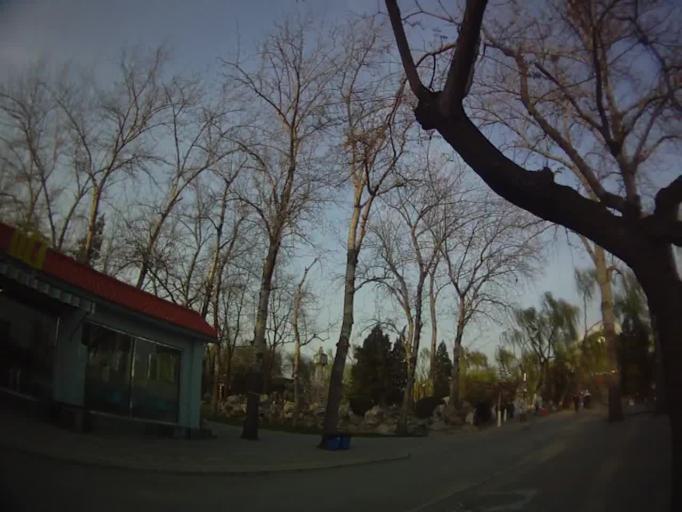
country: CN
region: Beijing
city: Longtan
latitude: 39.8782
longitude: 116.4315
